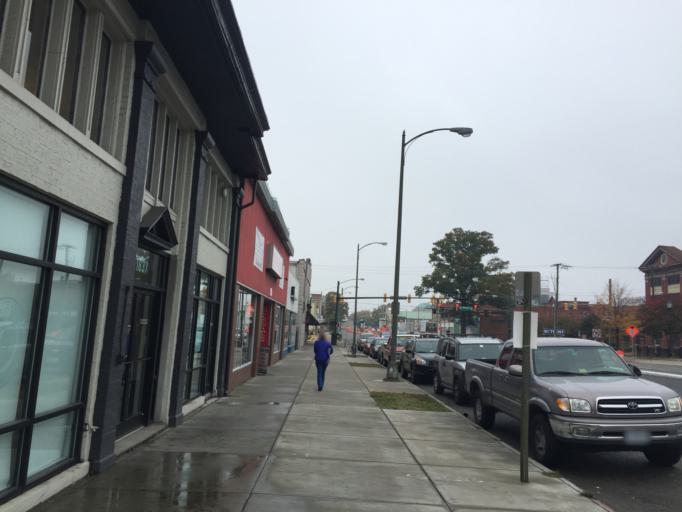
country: US
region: Virginia
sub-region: City of Richmond
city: Richmond
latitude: 37.5563
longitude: -77.4600
